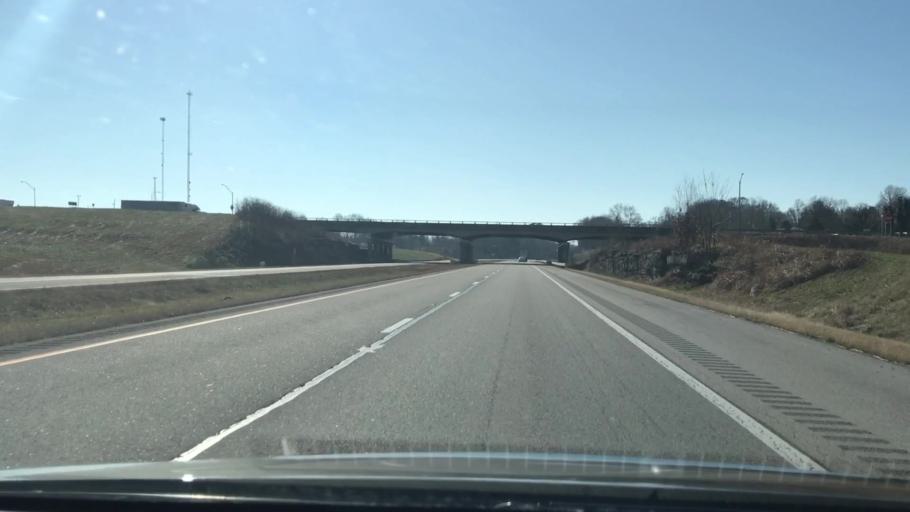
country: US
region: Kentucky
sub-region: Barren County
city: Glasgow
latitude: 36.9855
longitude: -85.8947
